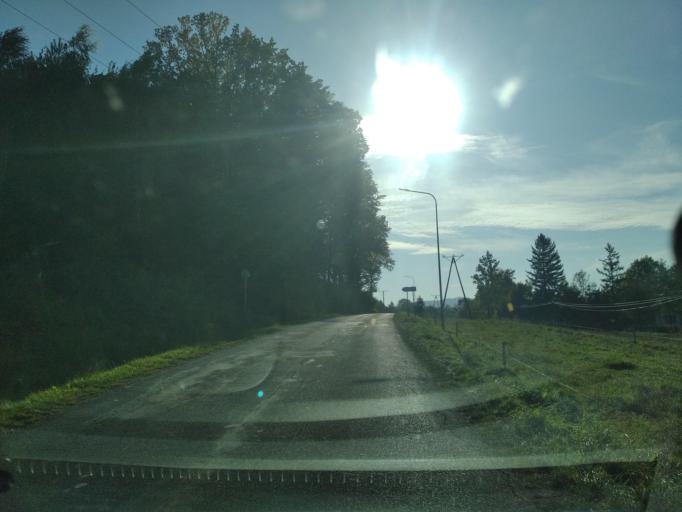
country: PL
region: Subcarpathian Voivodeship
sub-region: Powiat krosnienski
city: Sieniawa
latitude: 49.5712
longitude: 21.9414
